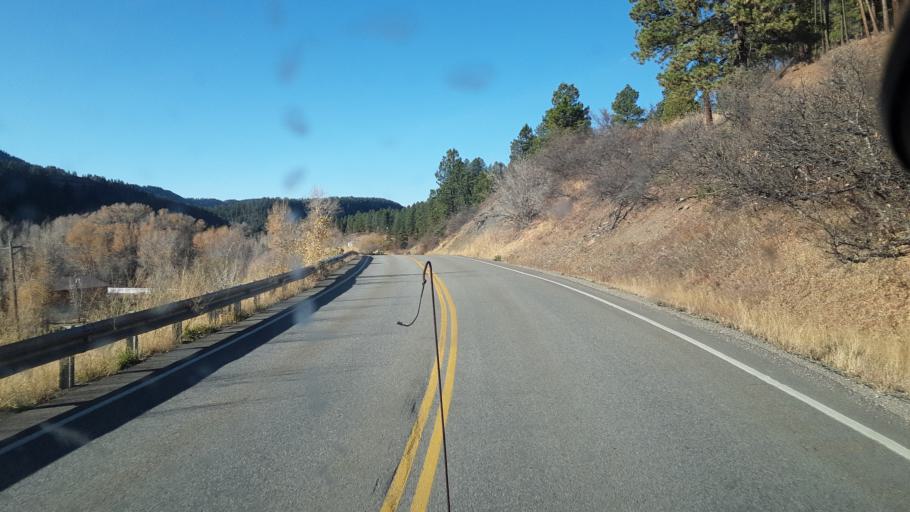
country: US
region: Colorado
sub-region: La Plata County
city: Bayfield
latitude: 37.3537
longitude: -107.6884
